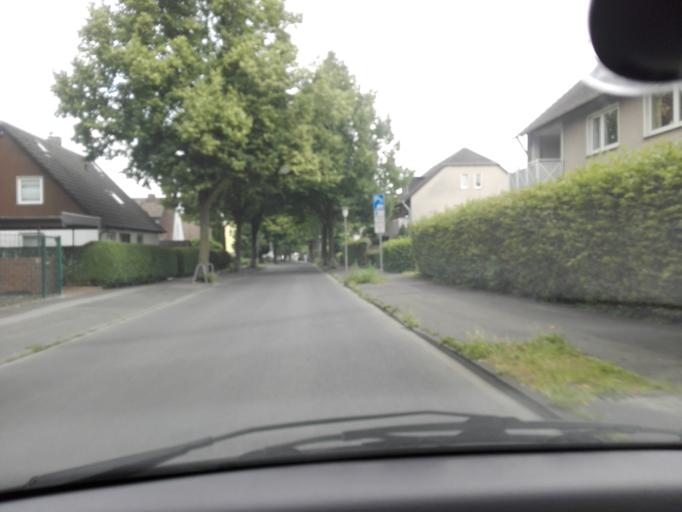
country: DE
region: North Rhine-Westphalia
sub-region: Regierungsbezirk Arnsberg
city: Unna
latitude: 51.5301
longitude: 7.6788
